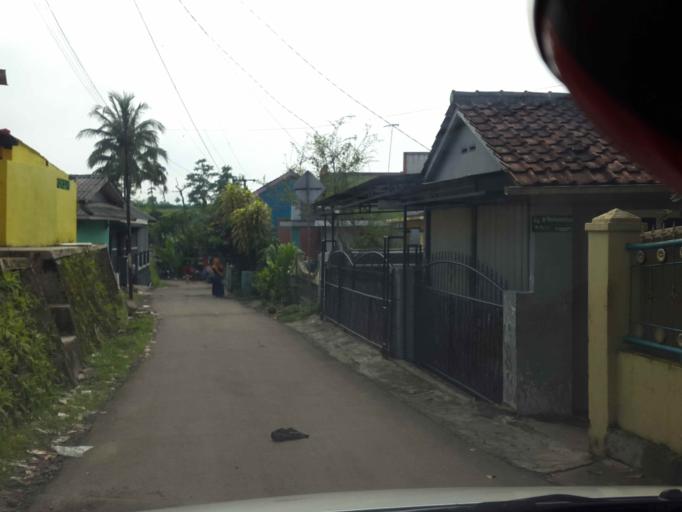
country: ID
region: West Java
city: Sukabumi
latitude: -6.8992
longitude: 106.9611
